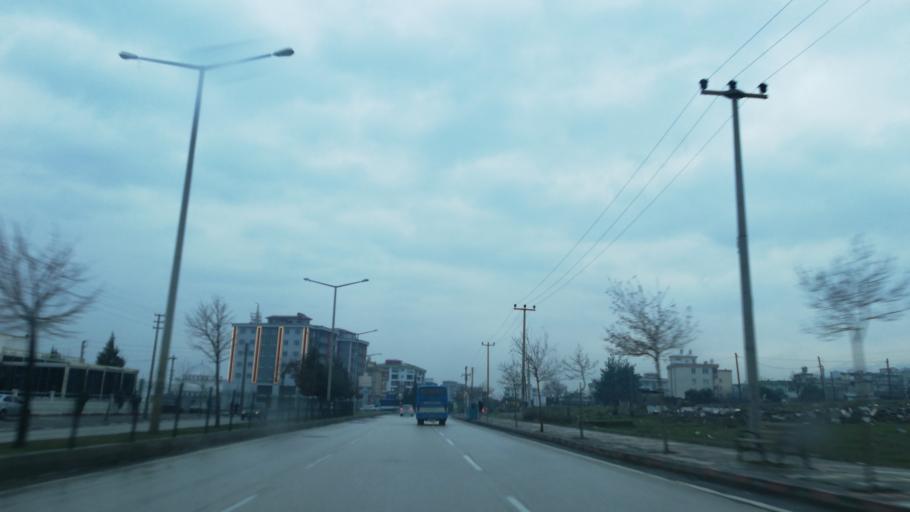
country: TR
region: Kahramanmaras
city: Kahramanmaras
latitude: 37.5825
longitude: 36.9757
